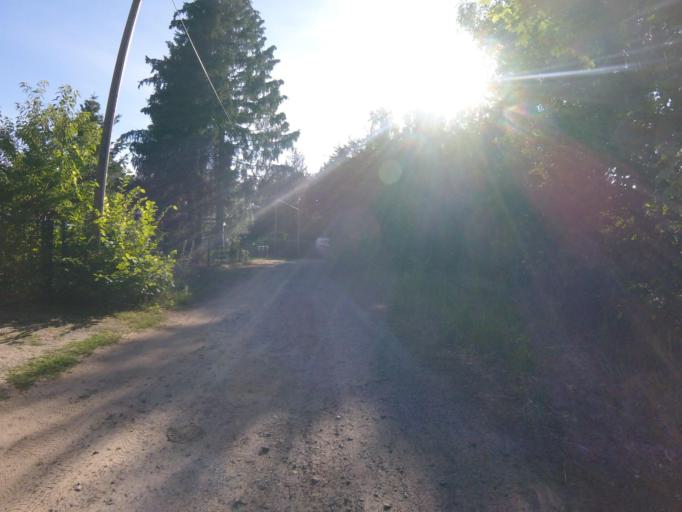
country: DE
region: Brandenburg
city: Wildau
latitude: 52.3230
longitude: 13.7197
